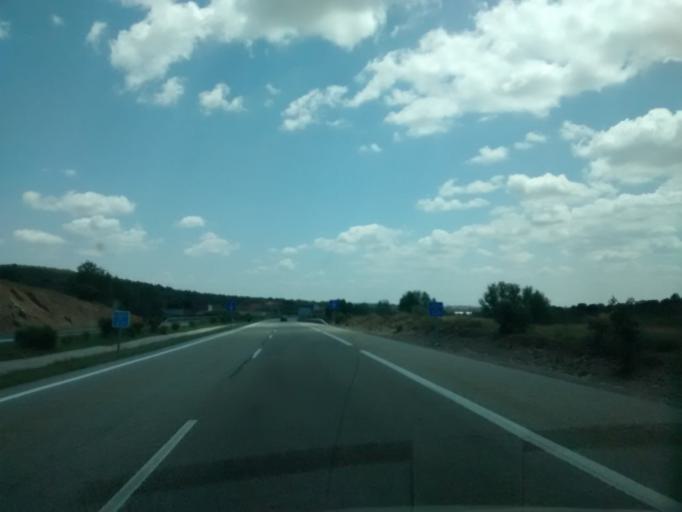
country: ES
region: Castille and Leon
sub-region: Provincia de Leon
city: Villaobispo de Otero
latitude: 42.4809
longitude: -6.1050
